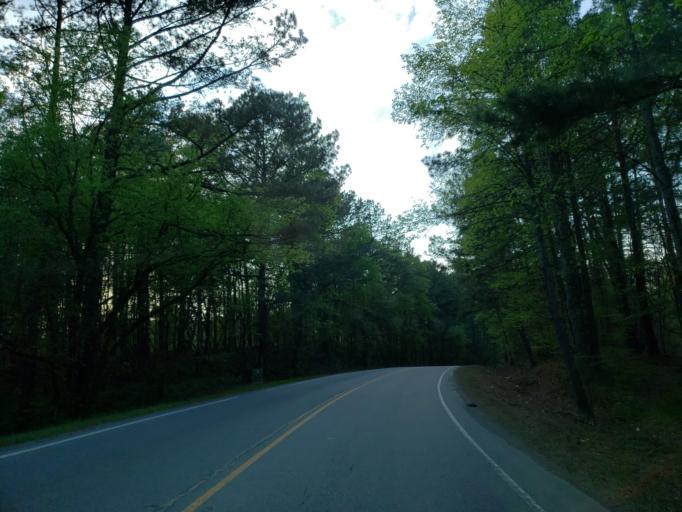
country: US
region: Georgia
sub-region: Cherokee County
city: Ball Ground
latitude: 34.2943
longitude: -84.3937
